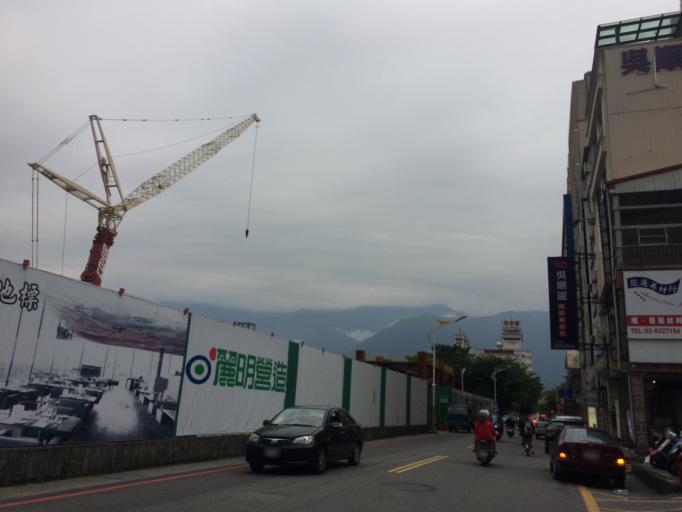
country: TW
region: Taiwan
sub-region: Hualien
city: Hualian
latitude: 23.9791
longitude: 121.6099
